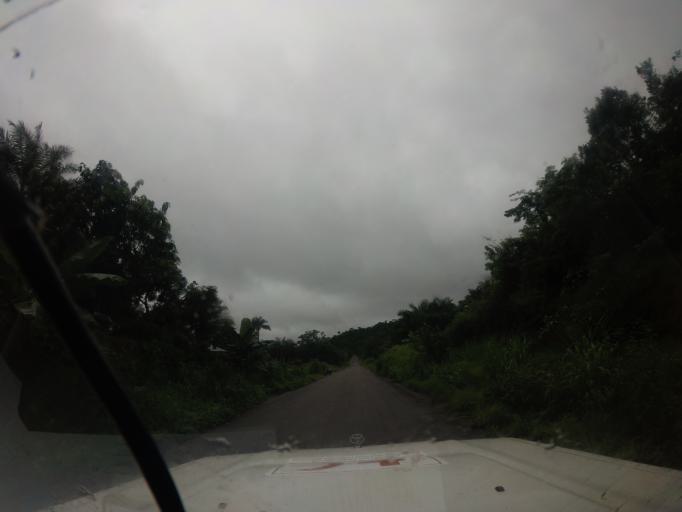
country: SL
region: Northern Province
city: Kabala
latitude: 9.4302
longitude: -11.7177
